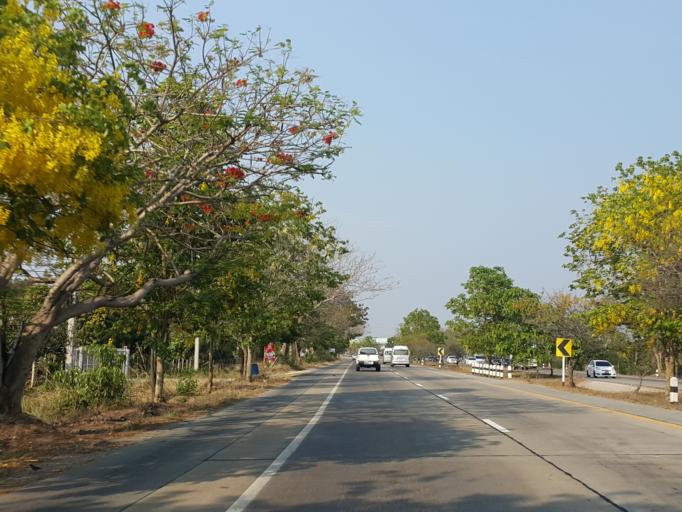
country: TH
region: Suphan Buri
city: Sam Chuk
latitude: 14.7894
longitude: 100.1015
